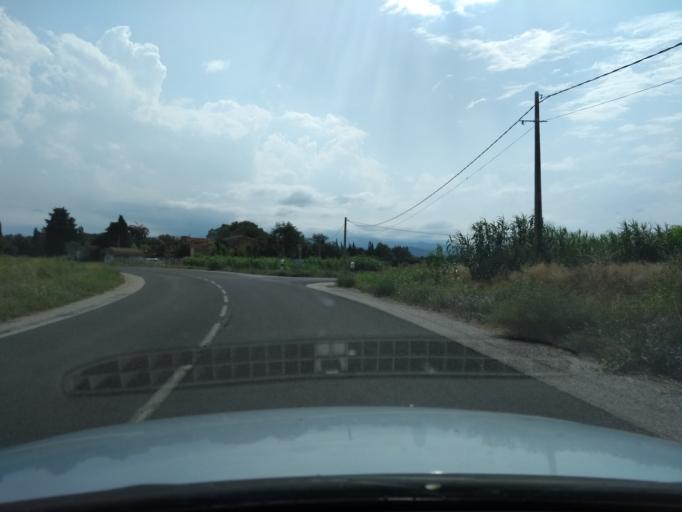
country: FR
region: Languedoc-Roussillon
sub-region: Departement des Pyrenees-Orientales
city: Pezilla-la-Riviere
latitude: 42.6916
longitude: 2.7524
